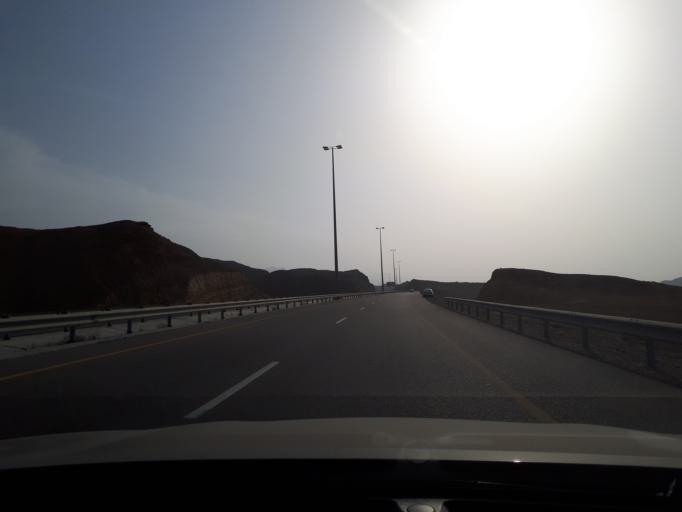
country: OM
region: Muhafazat Masqat
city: Muscat
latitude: 23.2070
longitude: 58.9162
